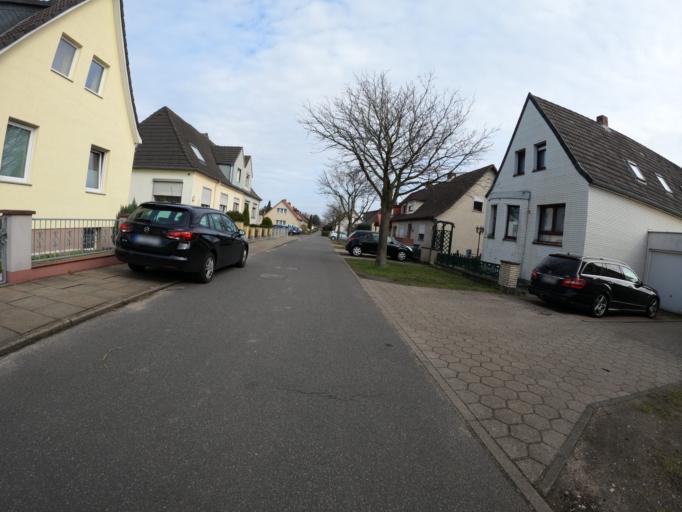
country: DE
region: Hamburg
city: Harburg
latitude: 53.4726
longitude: 9.9266
